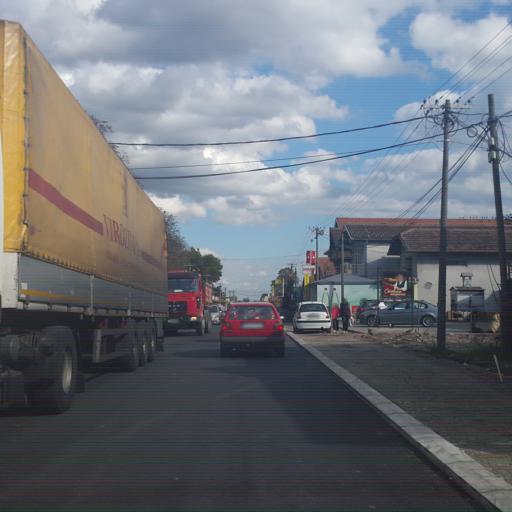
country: RS
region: Central Serbia
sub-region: Rasinski Okrug
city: Trstenik
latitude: 43.5778
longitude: 21.1504
